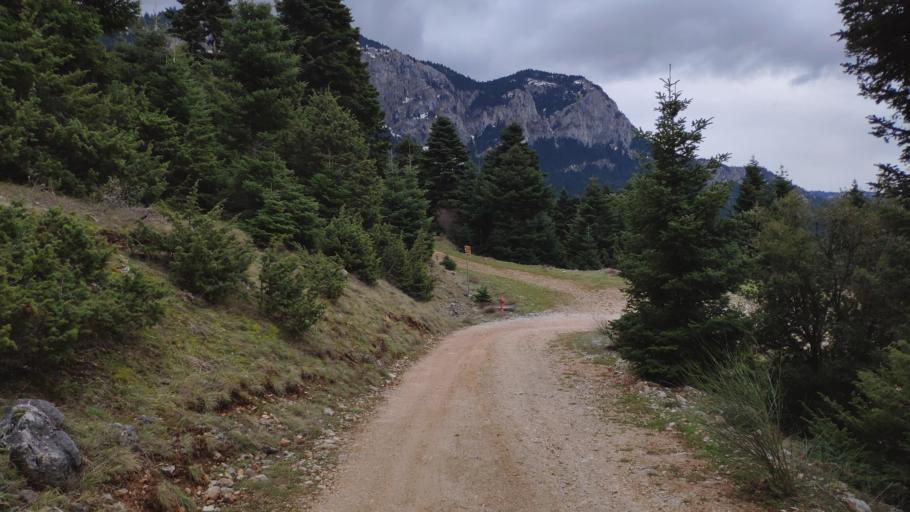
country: GR
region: Central Greece
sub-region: Nomos Fokidos
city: Amfissa
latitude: 38.6384
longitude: 22.4259
